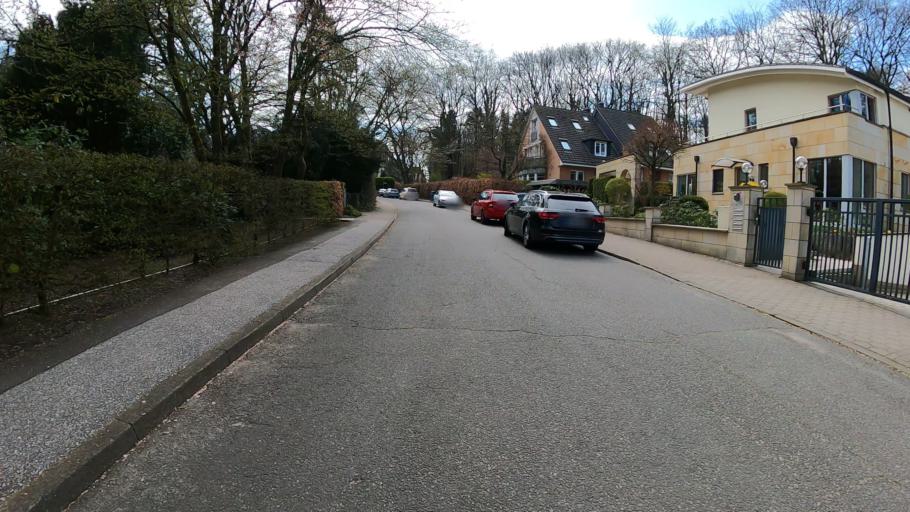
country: DE
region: Hamburg
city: Harburg
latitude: 53.4670
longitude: 9.9451
